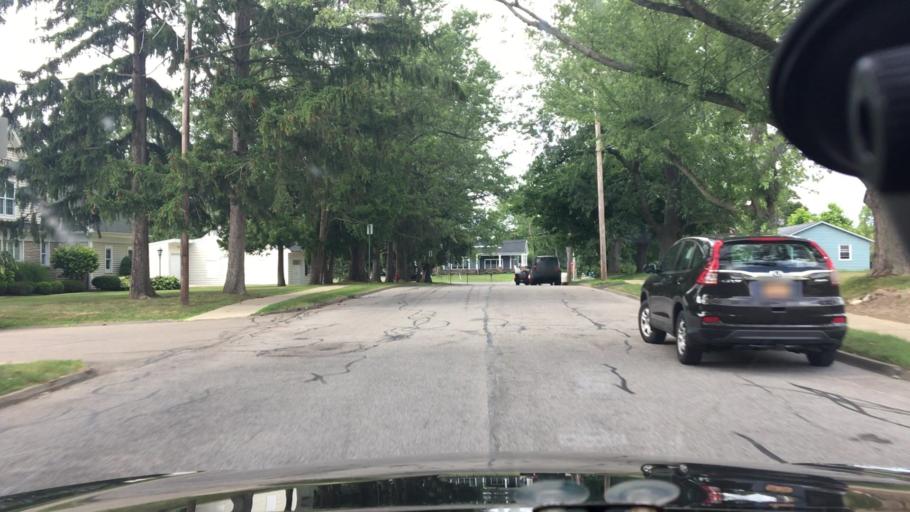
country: US
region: New York
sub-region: Erie County
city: Orchard Park
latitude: 42.7698
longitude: -78.7460
